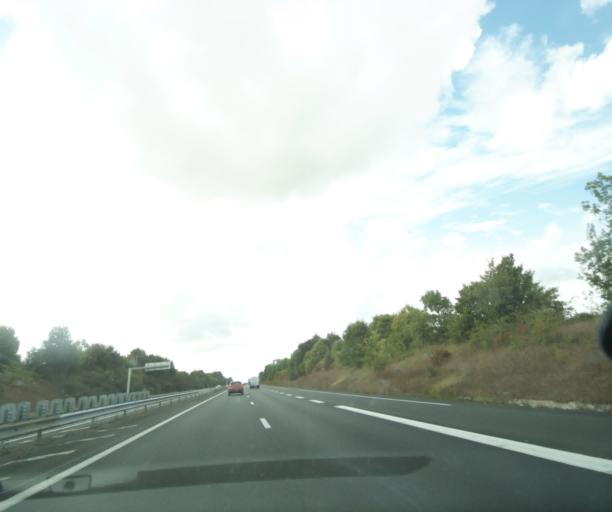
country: FR
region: Poitou-Charentes
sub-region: Departement de la Charente-Maritime
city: Chermignac
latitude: 45.7019
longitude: -0.6510
